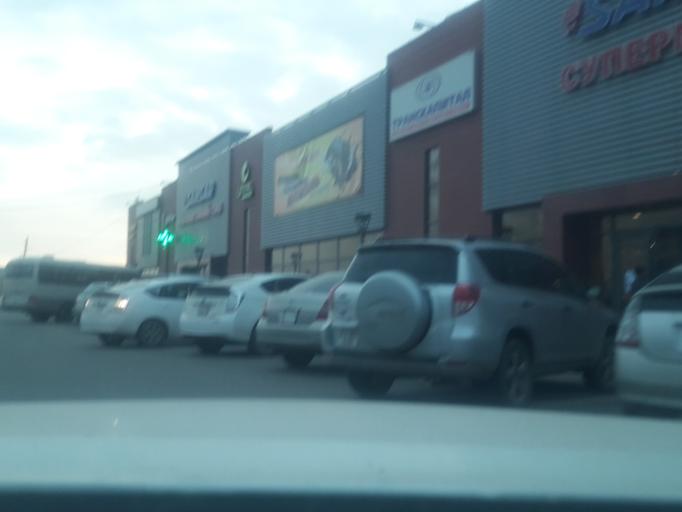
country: MN
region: Ulaanbaatar
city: Ulaanbaatar
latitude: 47.8718
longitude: 106.8310
